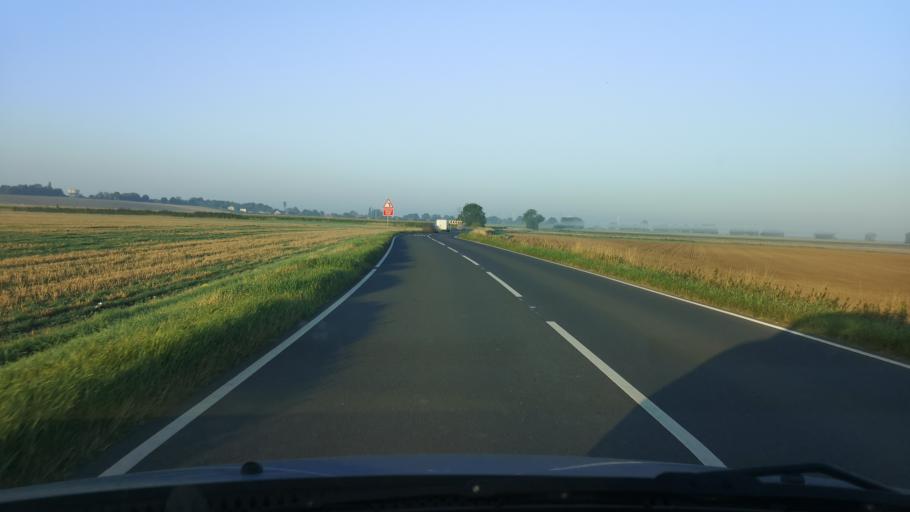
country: GB
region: England
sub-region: North Lincolnshire
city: Crowle
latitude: 53.6183
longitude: -0.8158
